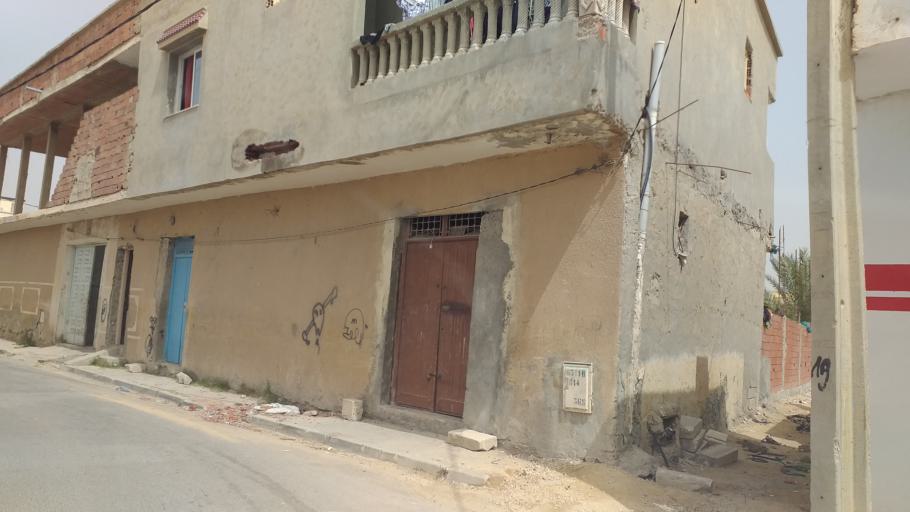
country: TN
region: Qabis
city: Gabes
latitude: 33.9410
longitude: 10.0616
